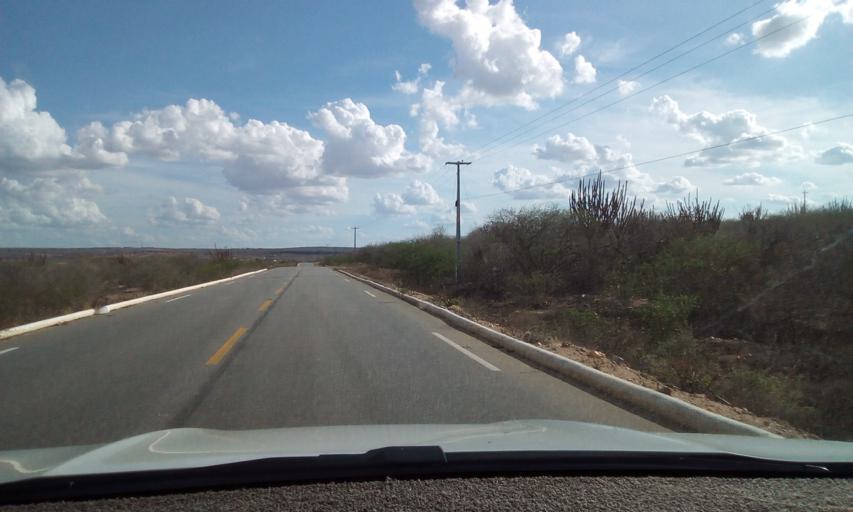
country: BR
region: Paraiba
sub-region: Soledade
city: Soledade
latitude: -6.8376
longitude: -36.4069
